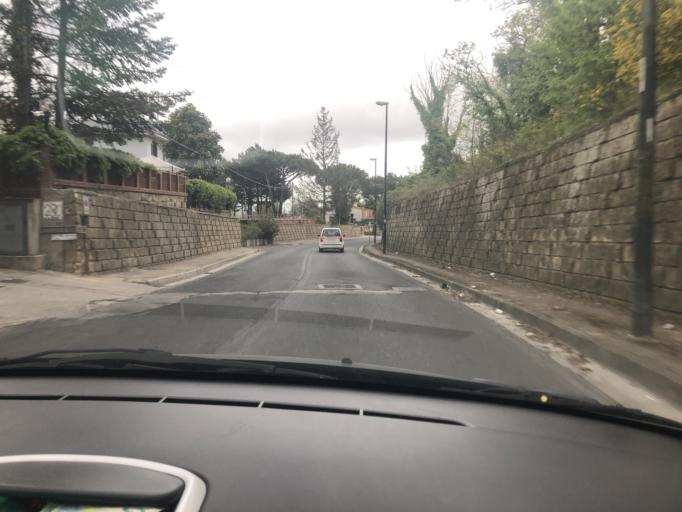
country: IT
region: Campania
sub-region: Provincia di Napoli
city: Torre Caracciolo
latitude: 40.8642
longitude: 14.1959
